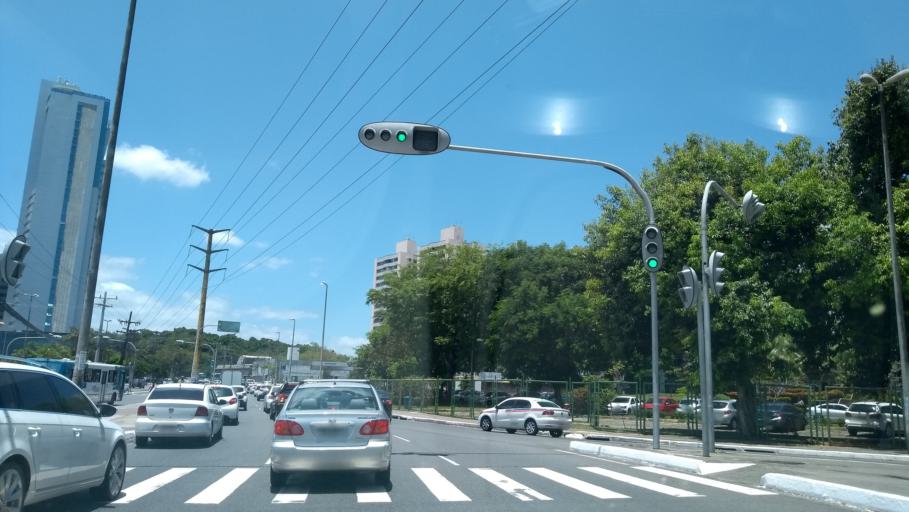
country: BR
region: Bahia
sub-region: Salvador
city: Salvador
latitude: -12.9834
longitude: -38.4507
